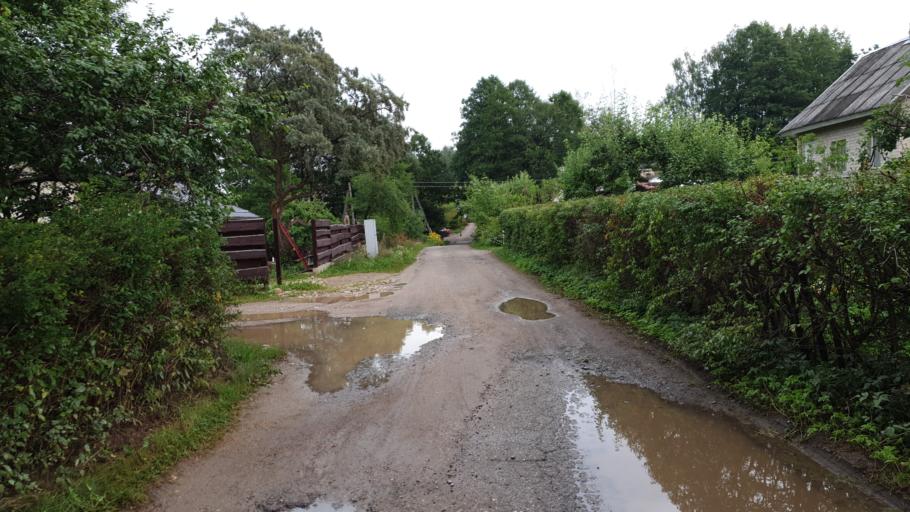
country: LT
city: Grigiskes
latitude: 54.7659
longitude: 25.0183
